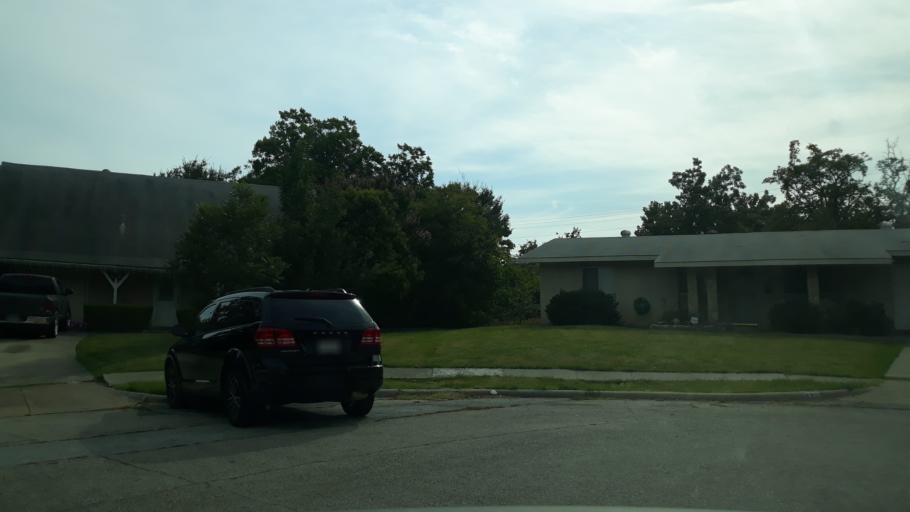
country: US
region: Texas
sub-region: Dallas County
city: Irving
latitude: 32.8479
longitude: -96.9900
